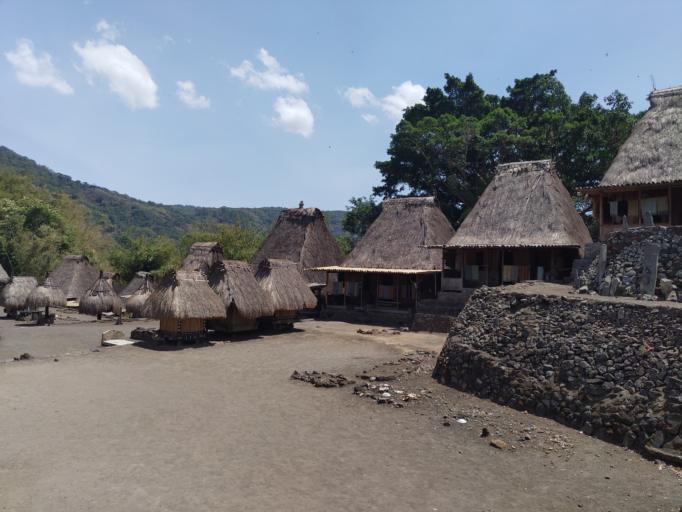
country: ID
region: East Nusa Tenggara
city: Gurusina
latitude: -8.8776
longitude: 120.9856
